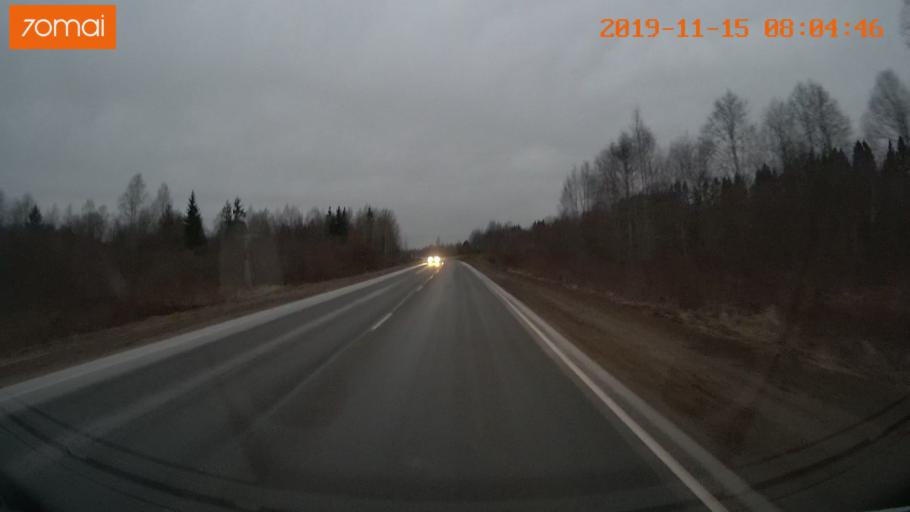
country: RU
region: Vologda
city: Cherepovets
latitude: 59.0114
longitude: 38.0703
